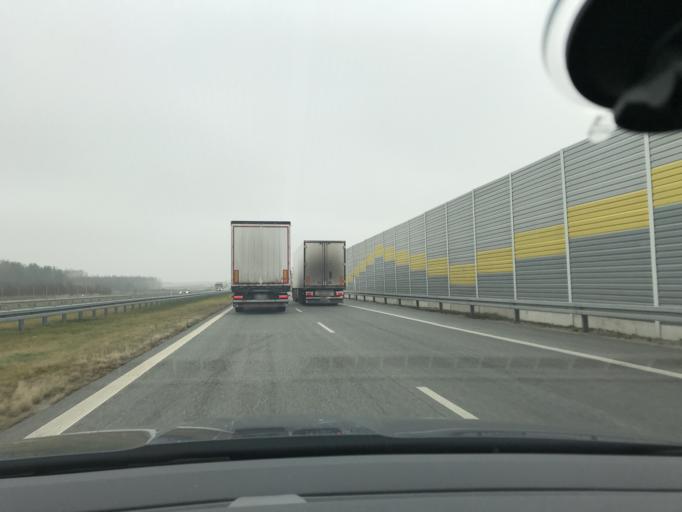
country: PL
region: Lodz Voivodeship
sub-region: Powiat laski
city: Lask
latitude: 51.5623
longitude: 19.1344
